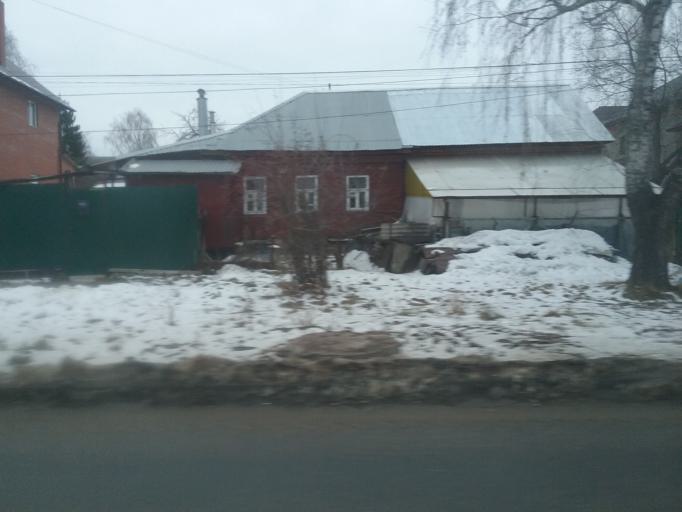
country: RU
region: Tula
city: Tula
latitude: 54.1651
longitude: 37.6125
